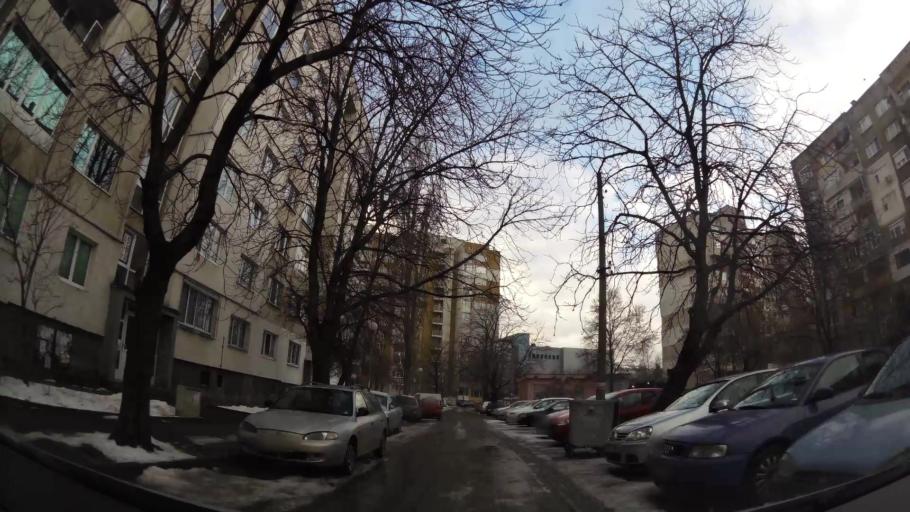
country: BG
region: Sofia-Capital
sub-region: Stolichna Obshtina
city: Sofia
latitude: 42.7066
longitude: 23.2913
